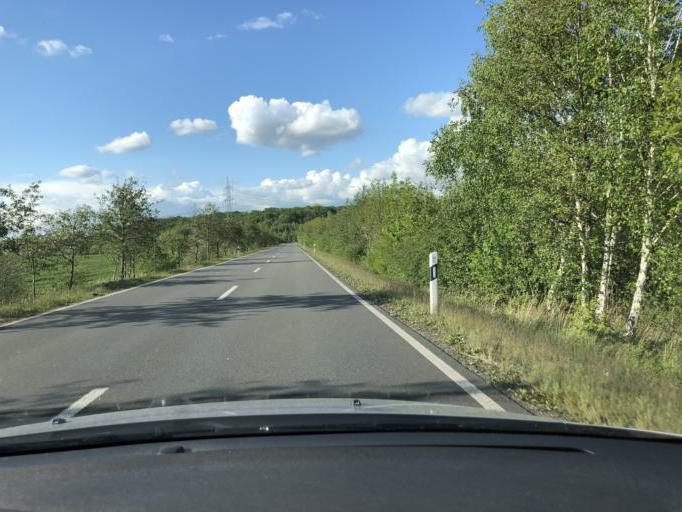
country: DE
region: Saxony
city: Neukieritzsch
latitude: 51.1792
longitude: 12.4196
